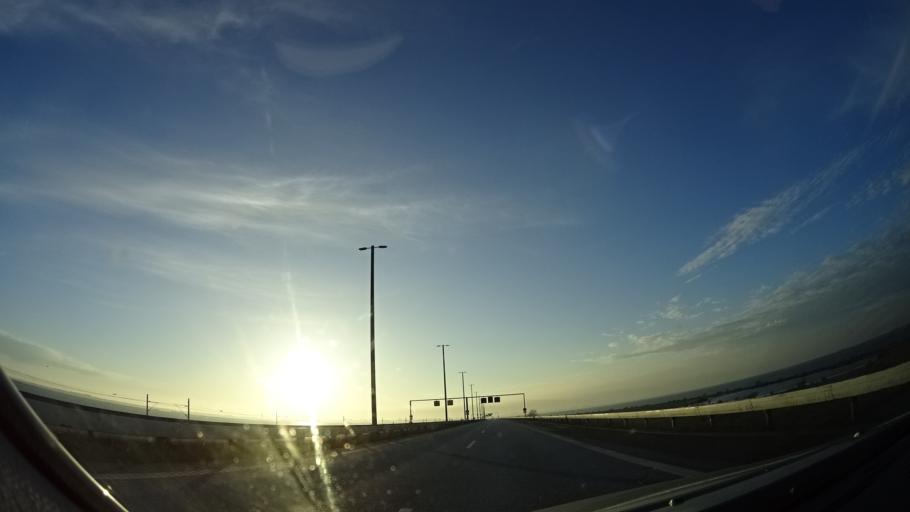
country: DK
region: Capital Region
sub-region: Dragor Kommune
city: Dragor
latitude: 55.6038
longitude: 12.7439
